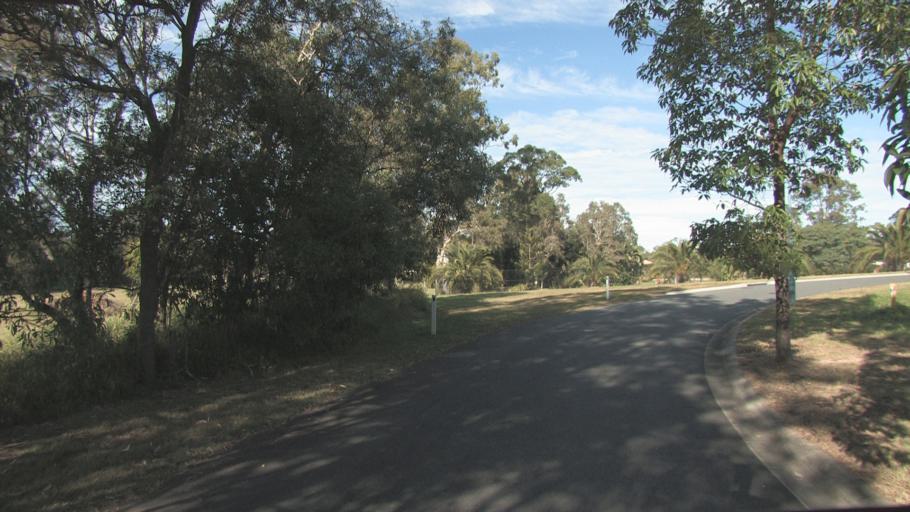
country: AU
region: Queensland
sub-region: Brisbane
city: Forest Lake
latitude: -27.6559
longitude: 152.9897
